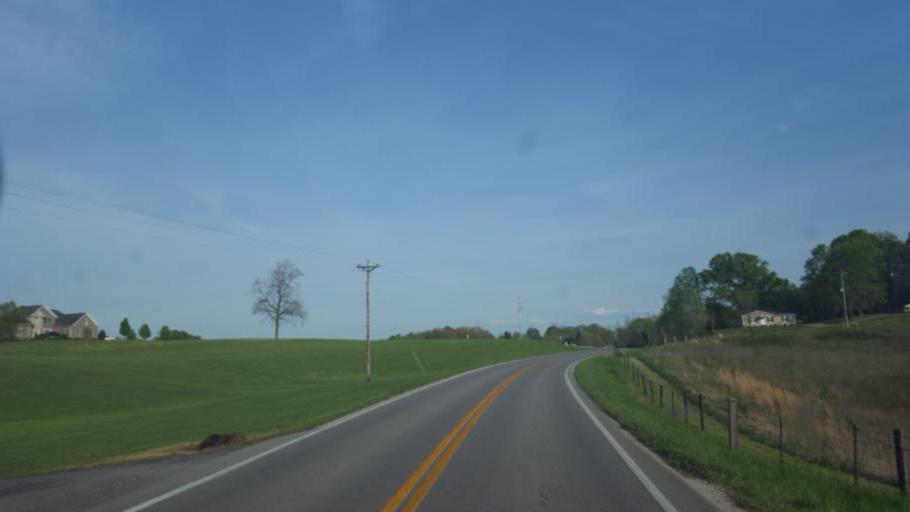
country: US
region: Kentucky
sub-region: Warren County
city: Plano
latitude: 36.9192
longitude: -86.2674
